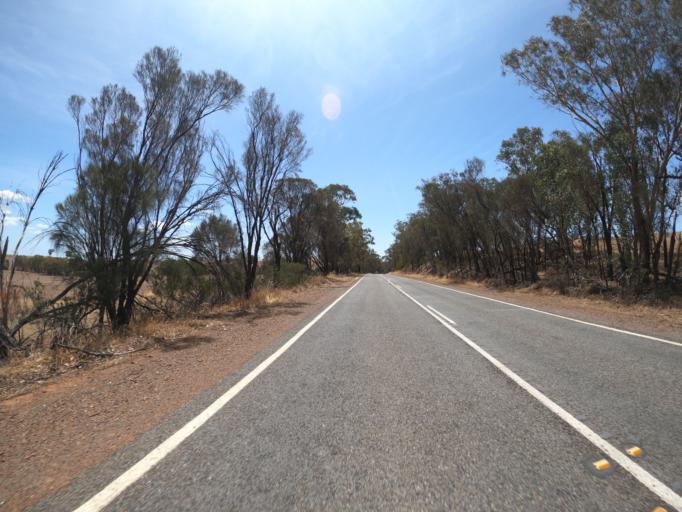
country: AU
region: Victoria
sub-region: Benalla
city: Benalla
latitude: -36.3383
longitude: 145.9590
